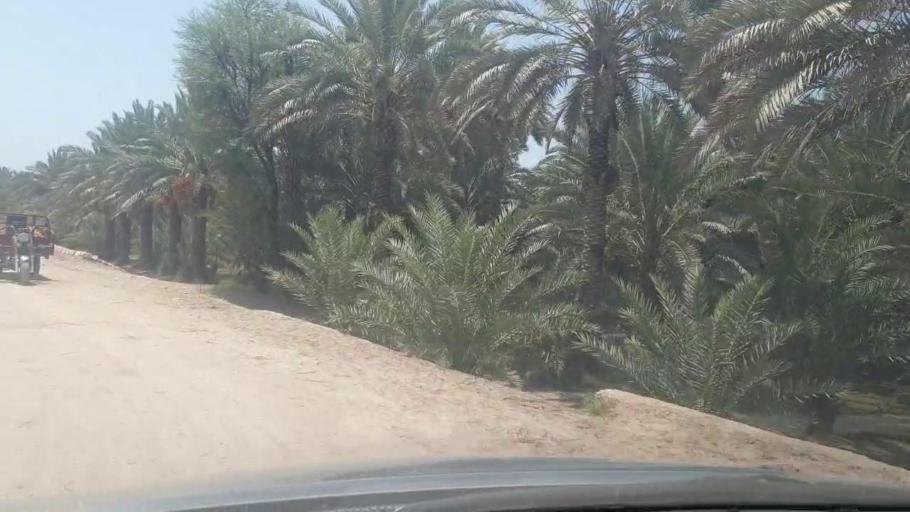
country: PK
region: Sindh
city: Kot Diji
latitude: 27.4174
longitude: 68.7448
